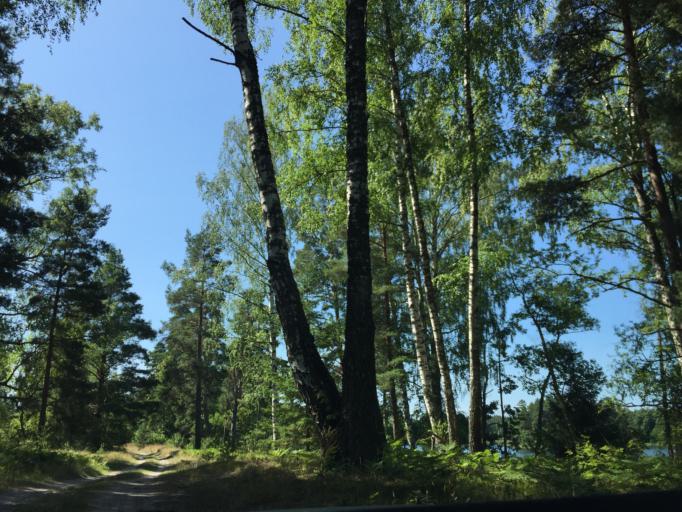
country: LV
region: Talsu Rajons
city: Stende
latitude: 57.1579
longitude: 22.3034
